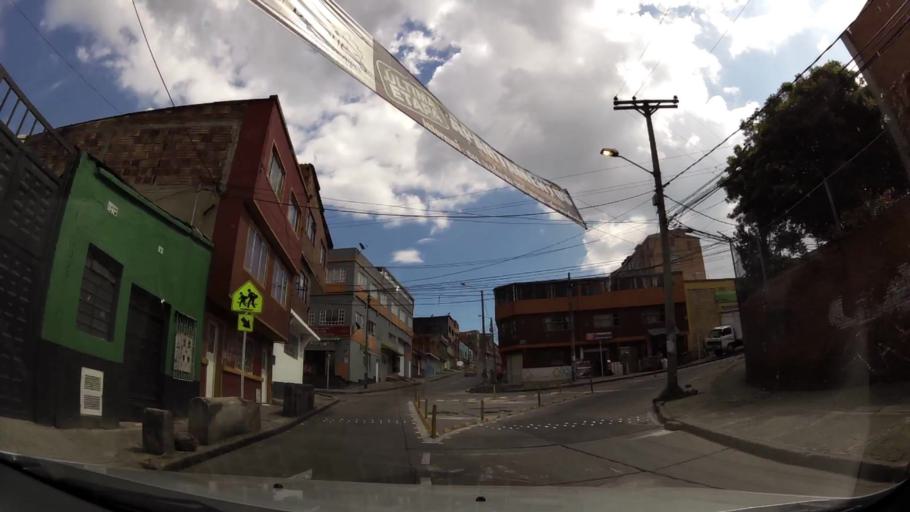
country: CO
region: Bogota D.C.
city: Bogota
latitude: 4.5645
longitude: -74.0871
